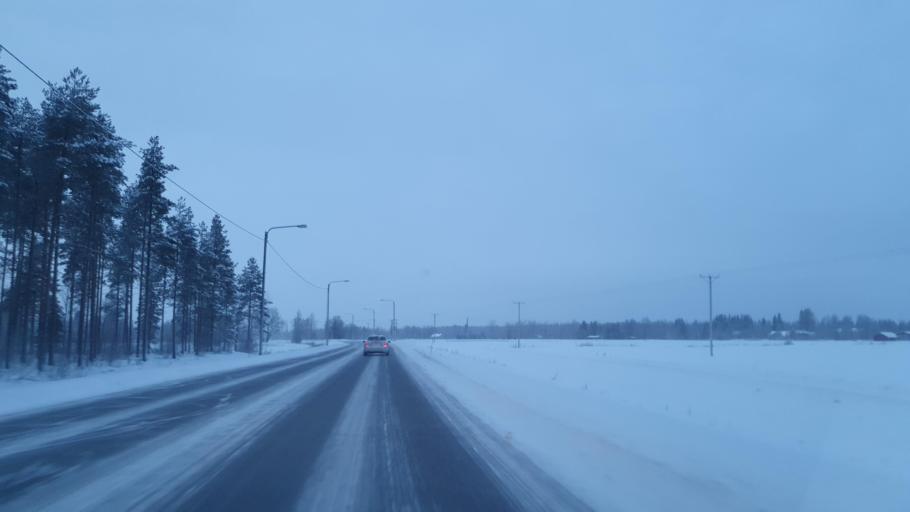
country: FI
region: Northern Ostrobothnia
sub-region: Oulunkaari
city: Utajaervi
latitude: 64.7802
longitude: 26.3649
